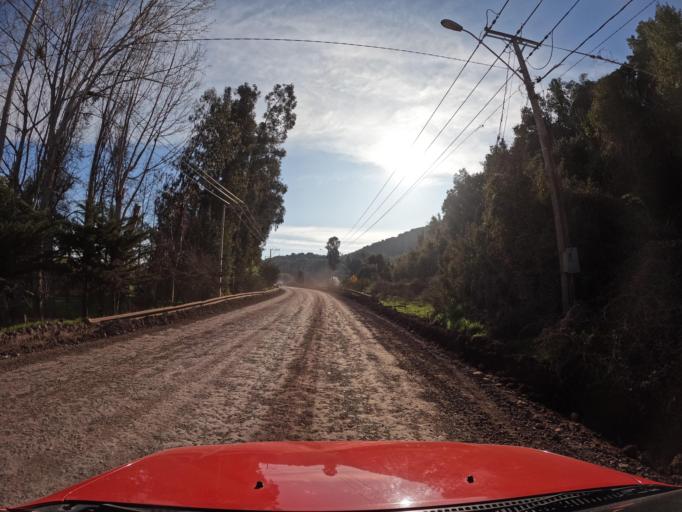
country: CL
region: Maule
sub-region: Provincia de Curico
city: Teno
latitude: -34.9685
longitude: -70.9422
